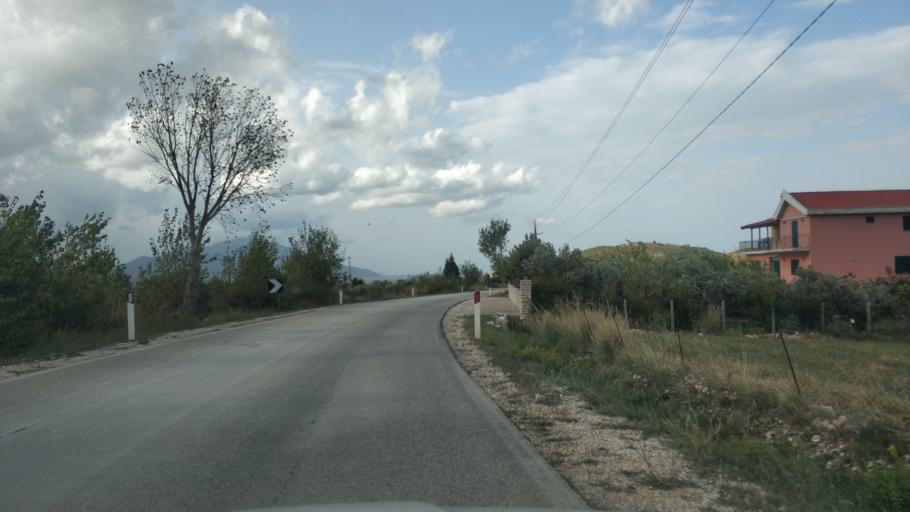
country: AL
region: Vlore
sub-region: Rrethi i Vlores
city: Orikum
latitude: 40.2885
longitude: 19.4937
